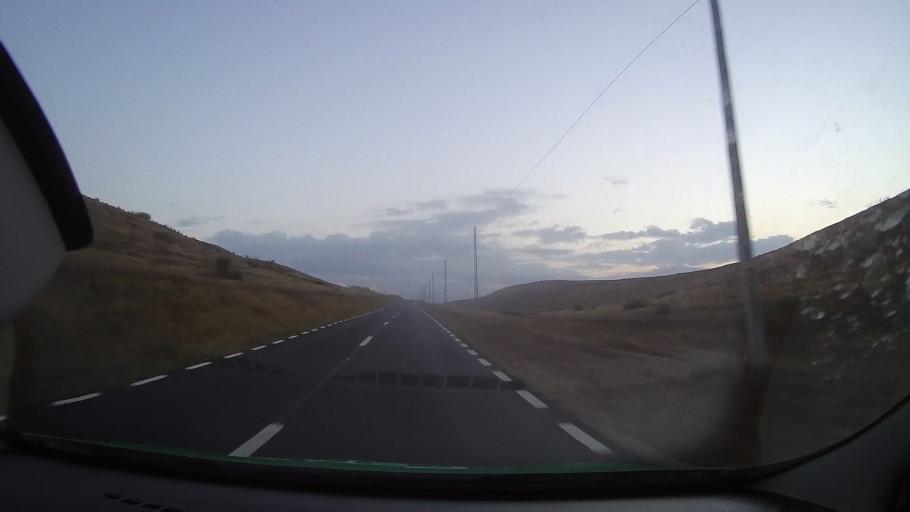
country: RO
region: Constanta
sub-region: Comuna Oltina
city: Oltina
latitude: 44.1481
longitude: 27.6670
